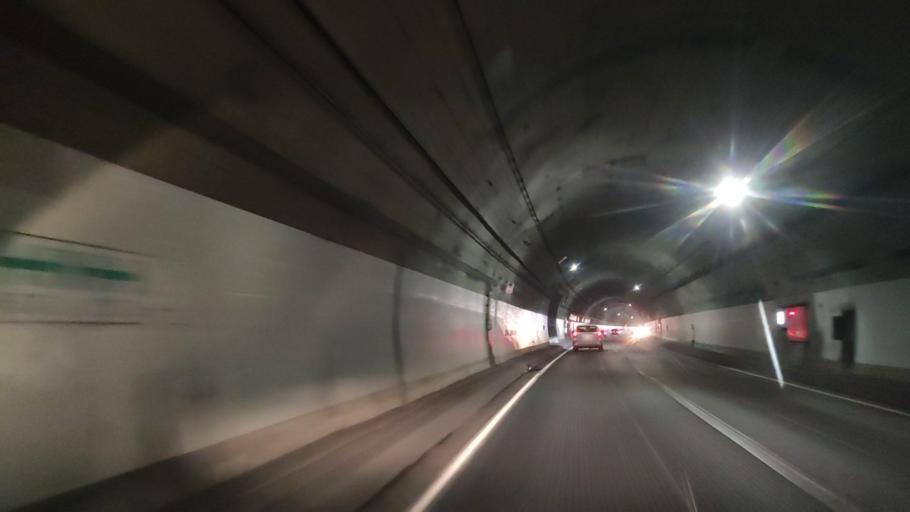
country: JP
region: Hokkaido
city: Rumoi
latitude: 43.7020
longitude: 141.3370
